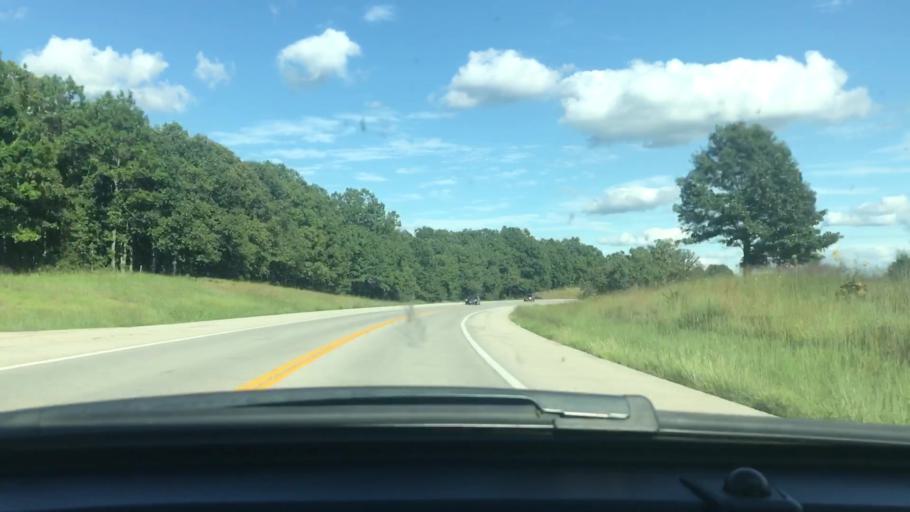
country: US
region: Missouri
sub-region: Howell County
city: West Plains
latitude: 36.6611
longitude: -91.7116
